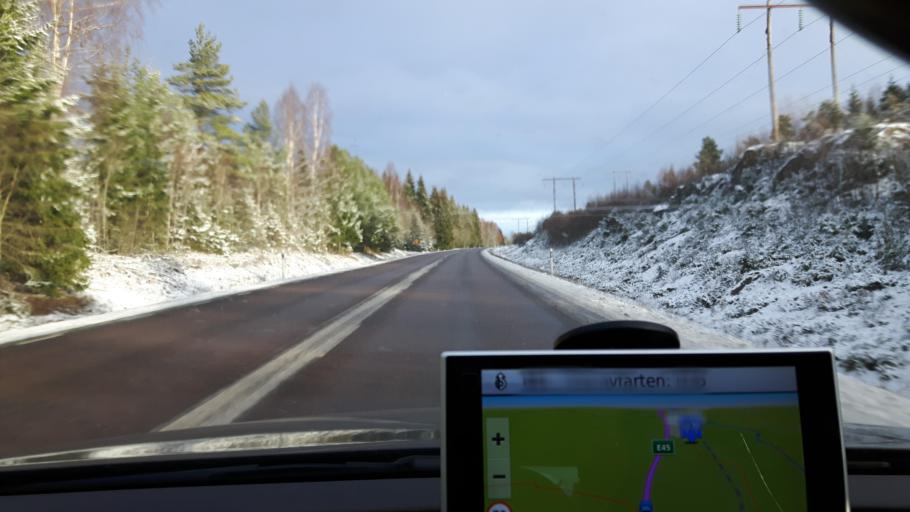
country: SE
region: Vaermland
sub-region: Karlstads Kommun
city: Valberg
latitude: 59.4083
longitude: 13.1826
